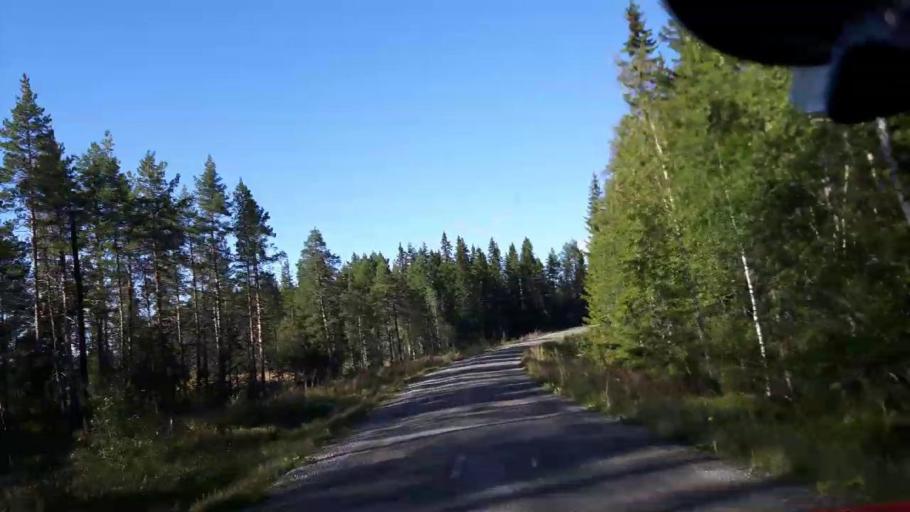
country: SE
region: Jaemtland
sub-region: Ragunda Kommun
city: Hammarstrand
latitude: 63.5231
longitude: 16.0559
